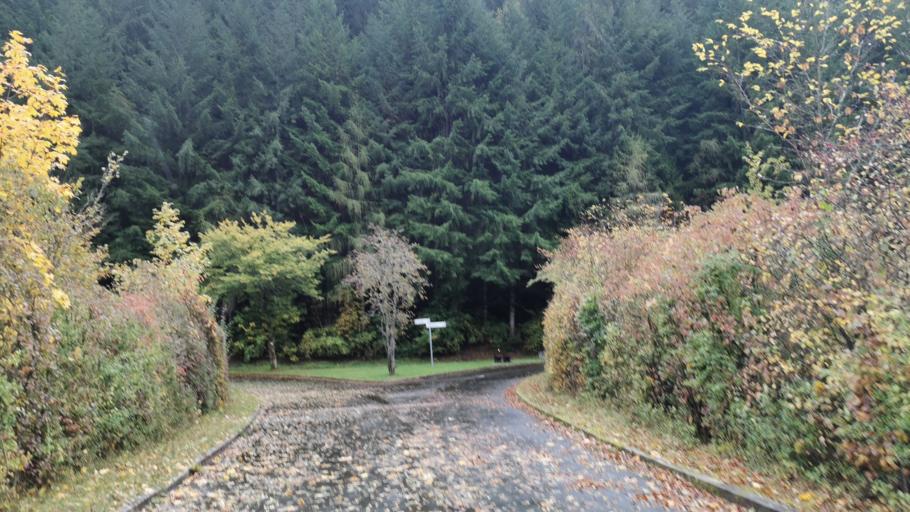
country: DE
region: Bavaria
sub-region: Upper Franconia
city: Nordhalben
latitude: 50.3551
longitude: 11.4881
